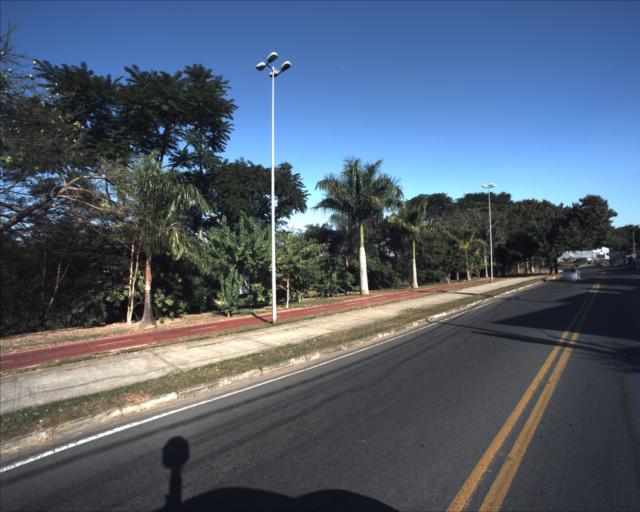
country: BR
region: Sao Paulo
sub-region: Sorocaba
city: Sorocaba
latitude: -23.4722
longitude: -47.4426
